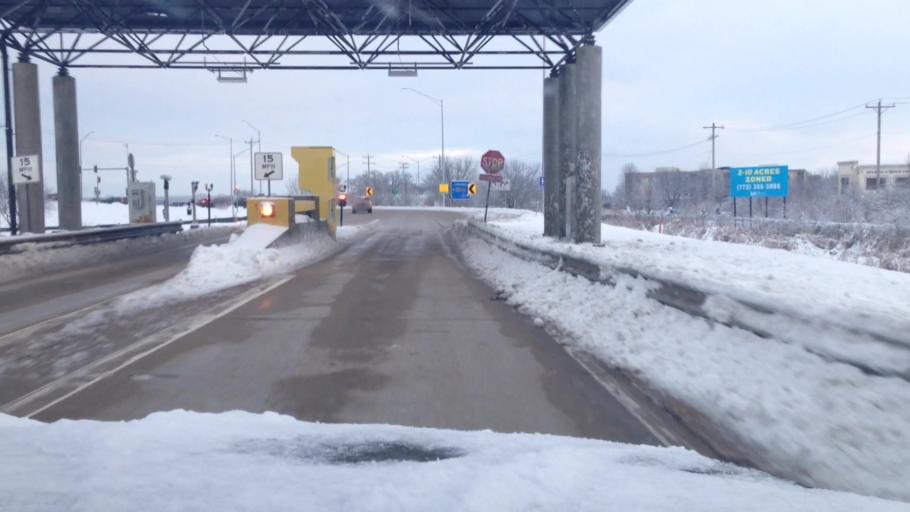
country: US
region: Illinois
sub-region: Kane County
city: Sleepy Hollow
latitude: 42.0803
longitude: -88.3371
